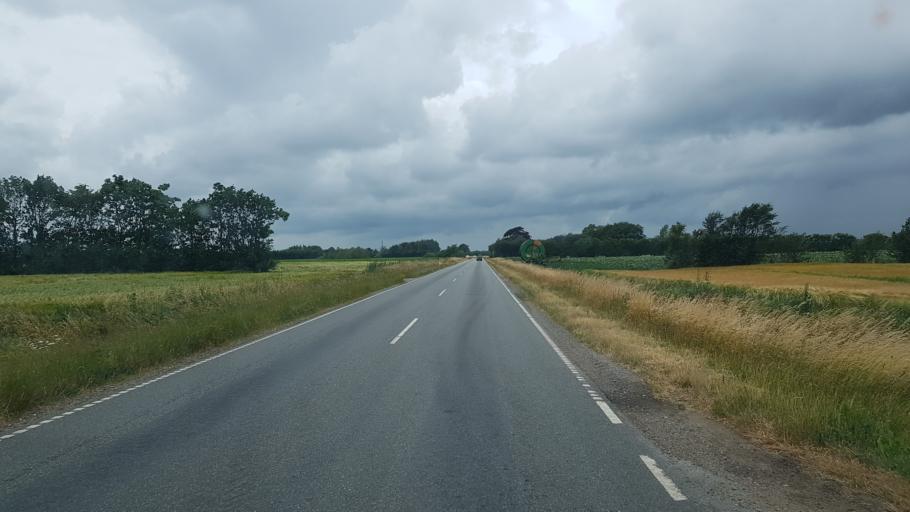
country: DK
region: South Denmark
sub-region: Kolding Kommune
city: Vamdrup
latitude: 55.4357
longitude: 9.2061
